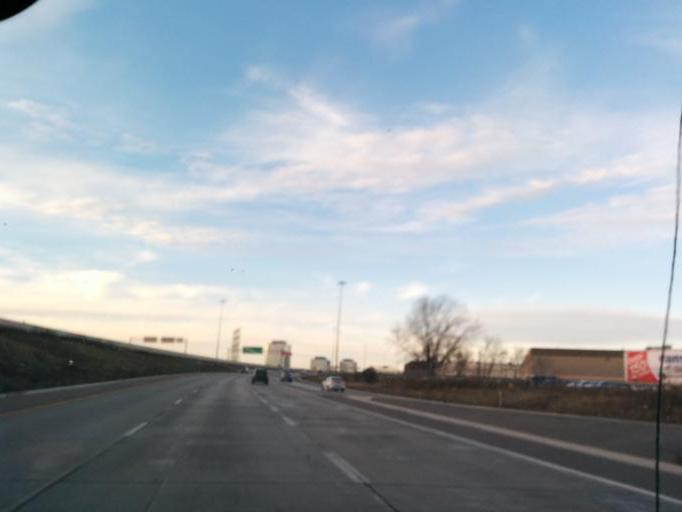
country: CA
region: Ontario
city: Etobicoke
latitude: 43.6166
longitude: -79.5503
